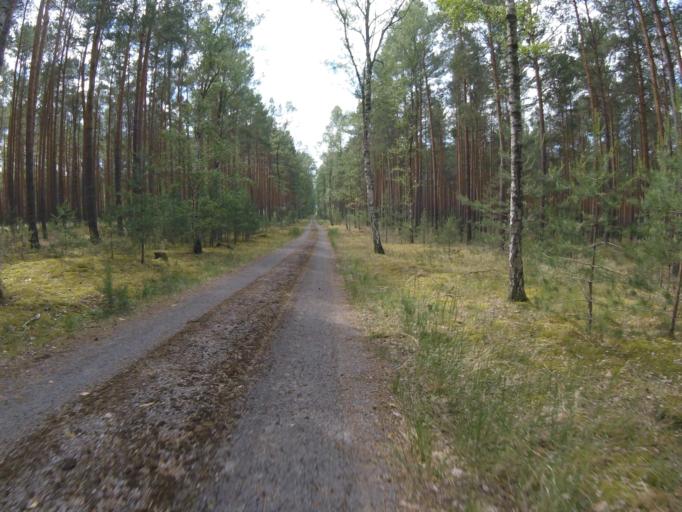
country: DE
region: Brandenburg
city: Halbe
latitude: 52.1215
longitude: 13.6697
